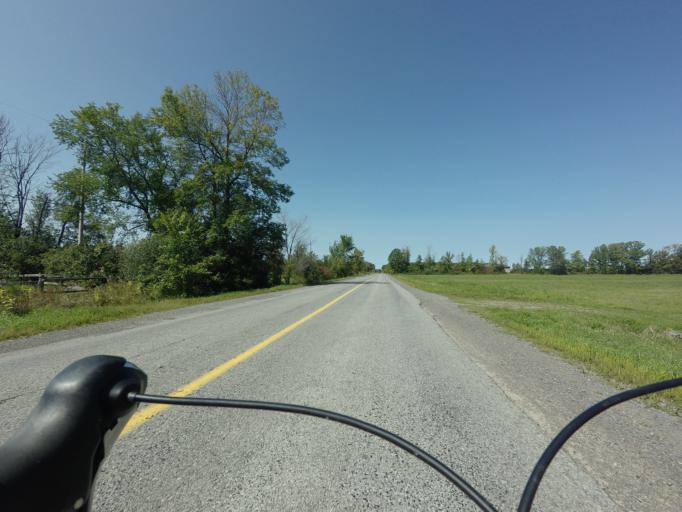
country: CA
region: Ontario
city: Bells Corners
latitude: 45.4287
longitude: -76.0547
